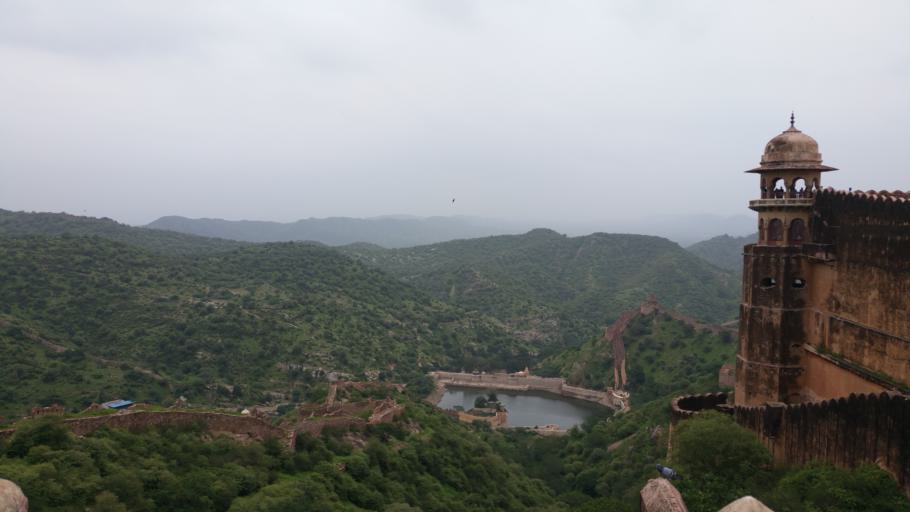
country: IN
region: Rajasthan
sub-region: Jaipur
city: Jaipur
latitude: 26.9855
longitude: 75.8455
